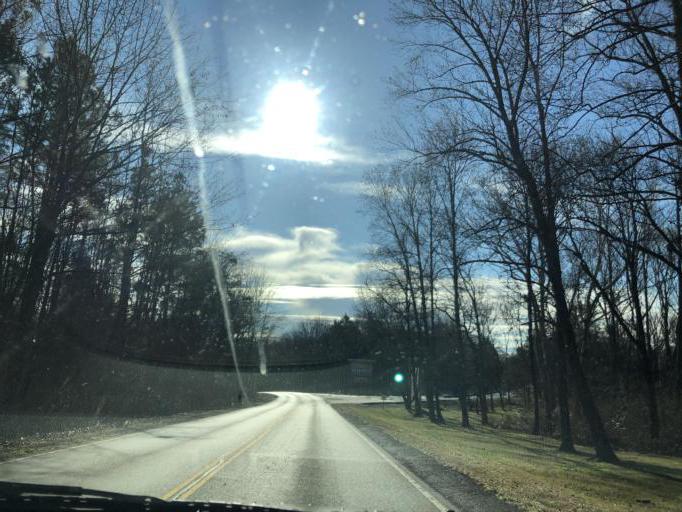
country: US
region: Tennessee
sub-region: Wilson County
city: Green Hill
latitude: 36.1629
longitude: -86.6003
